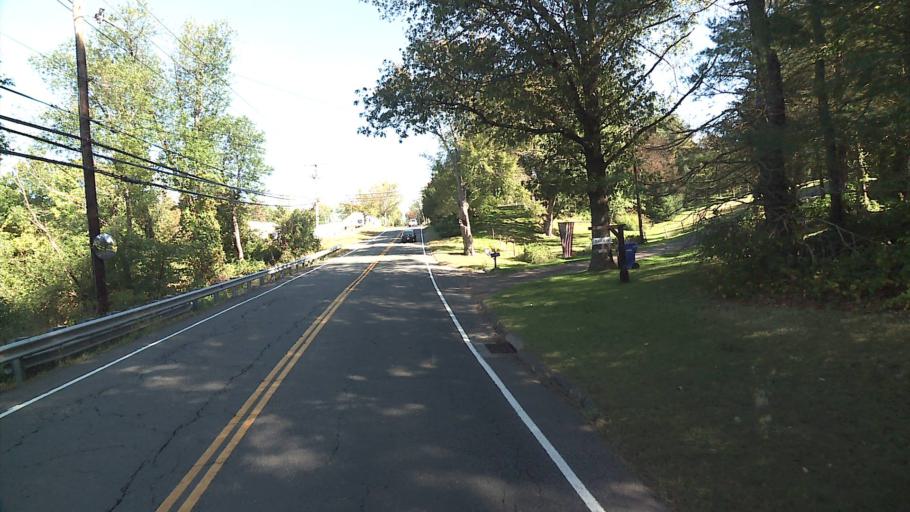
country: US
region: Connecticut
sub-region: Tolland County
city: Ellington
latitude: 41.9309
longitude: -72.4559
